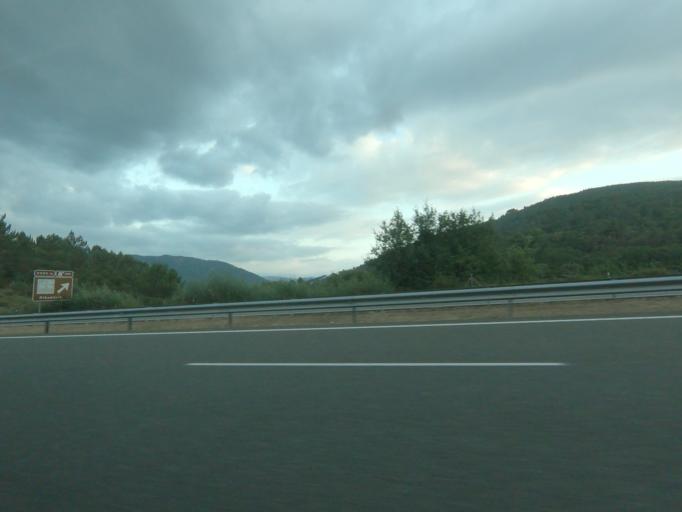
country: ES
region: Galicia
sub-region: Provincia de Ourense
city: Ribadavia
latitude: 42.3048
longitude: -8.1496
